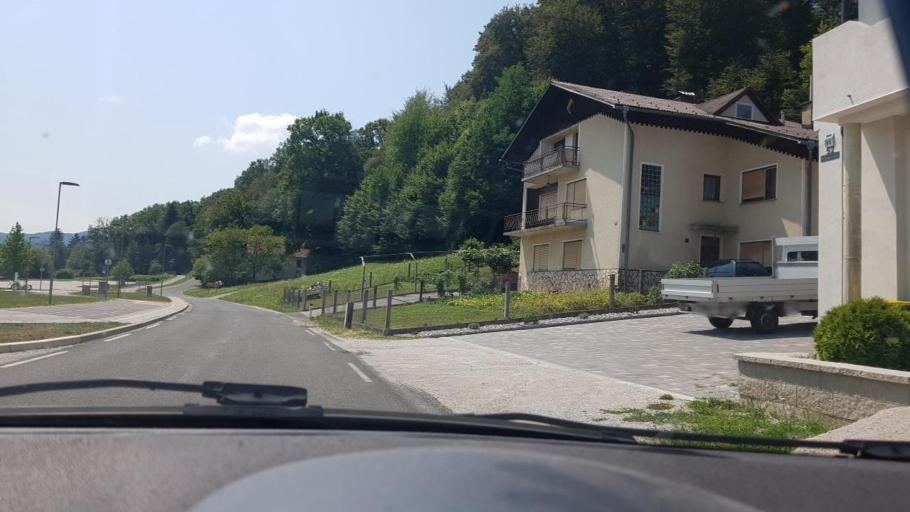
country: SI
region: Rogaska Slatina
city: Rogaska Slatina
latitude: 46.2209
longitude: 15.6393
